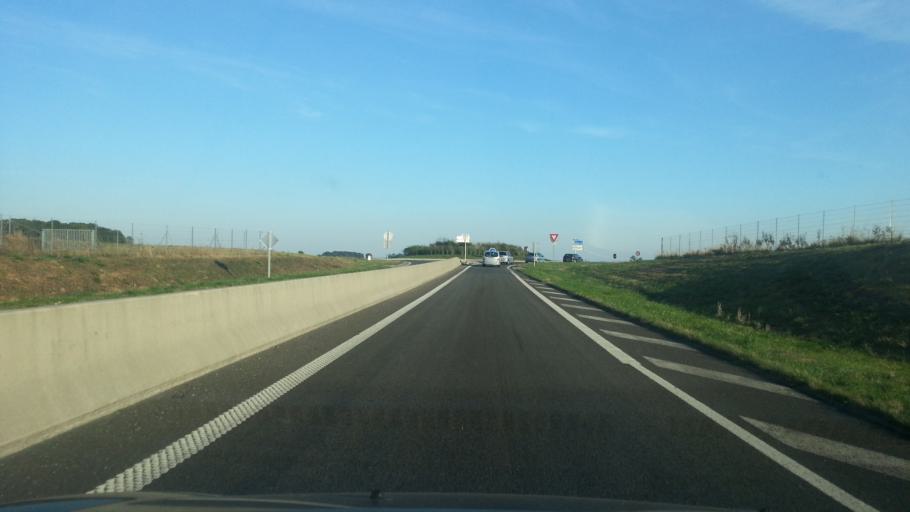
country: FR
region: Picardie
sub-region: Departement de l'Oise
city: Catenoy
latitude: 49.3796
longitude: 2.5215
